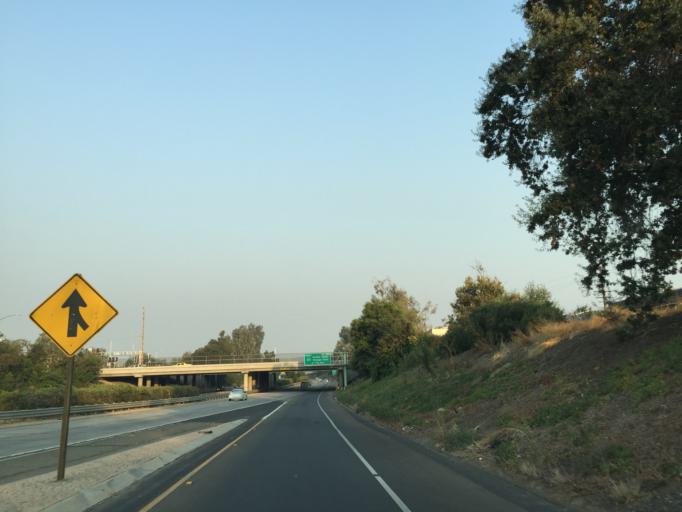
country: US
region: California
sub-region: Tulare County
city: Visalia
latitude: 36.3267
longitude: -119.2765
